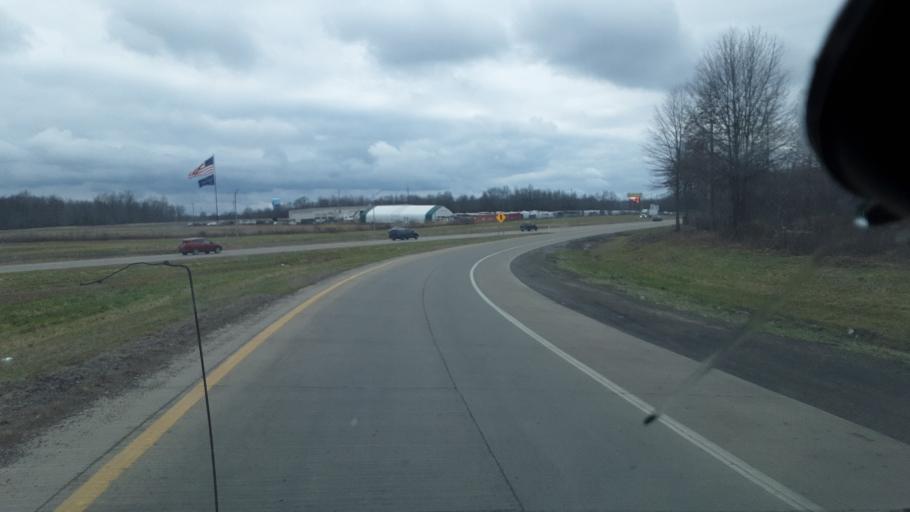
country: US
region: Ohio
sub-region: Trumbull County
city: Lordstown
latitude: 41.1080
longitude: -80.8890
